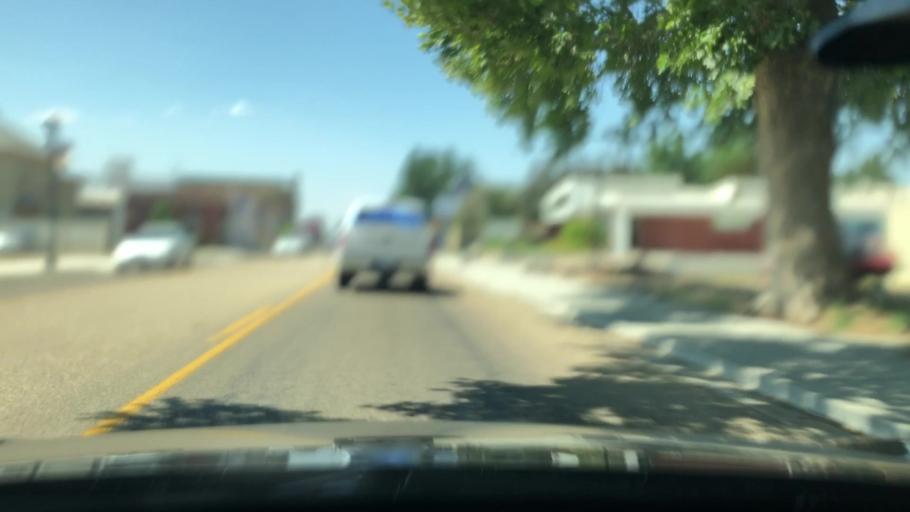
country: US
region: Idaho
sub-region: Canyon County
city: Parma
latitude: 43.7851
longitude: -116.9431
